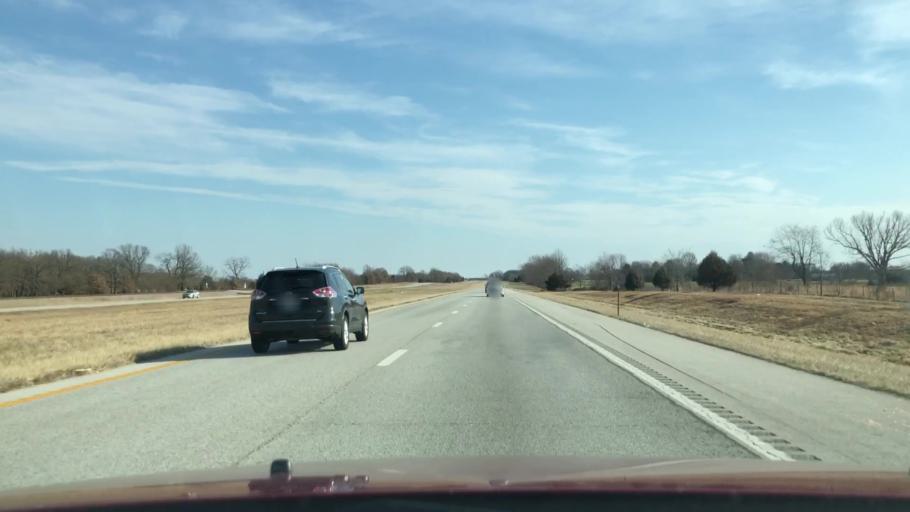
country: US
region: Missouri
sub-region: Webster County
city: Rogersville
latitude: 37.1225
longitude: -92.9971
